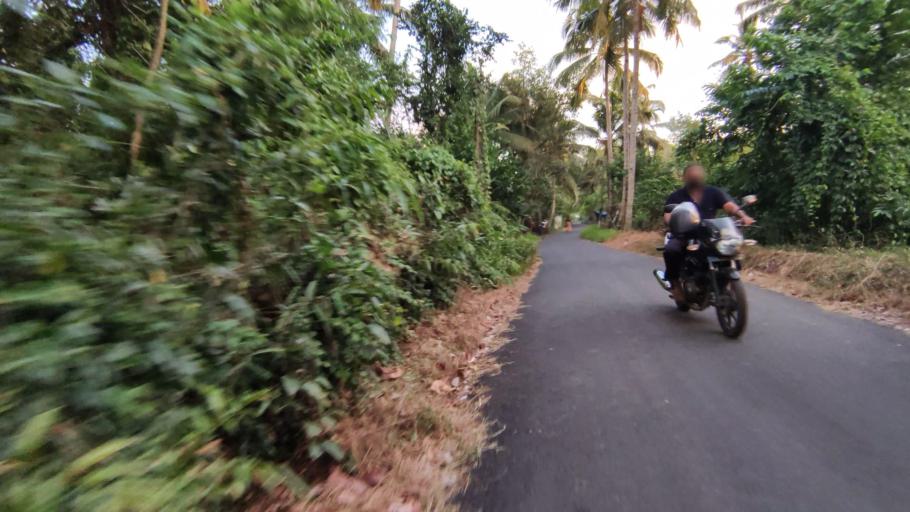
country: IN
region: Kerala
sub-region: Kottayam
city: Kottayam
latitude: 9.5788
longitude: 76.4468
